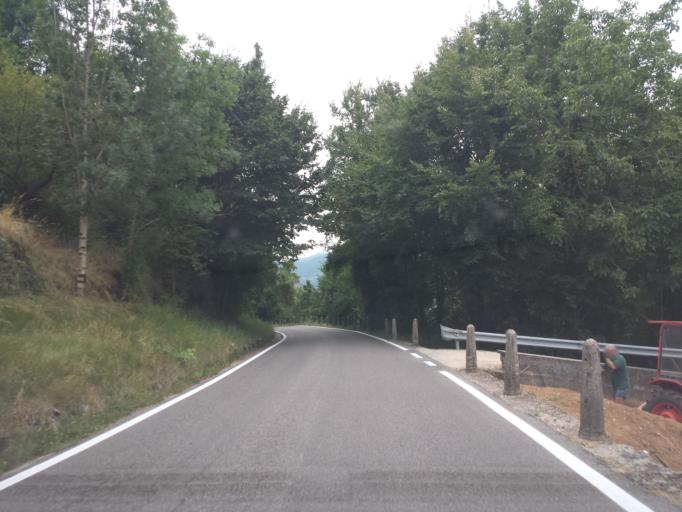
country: IT
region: Veneto
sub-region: Provincia di Vicenza
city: Valdagno
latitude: 45.6417
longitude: 11.3190
